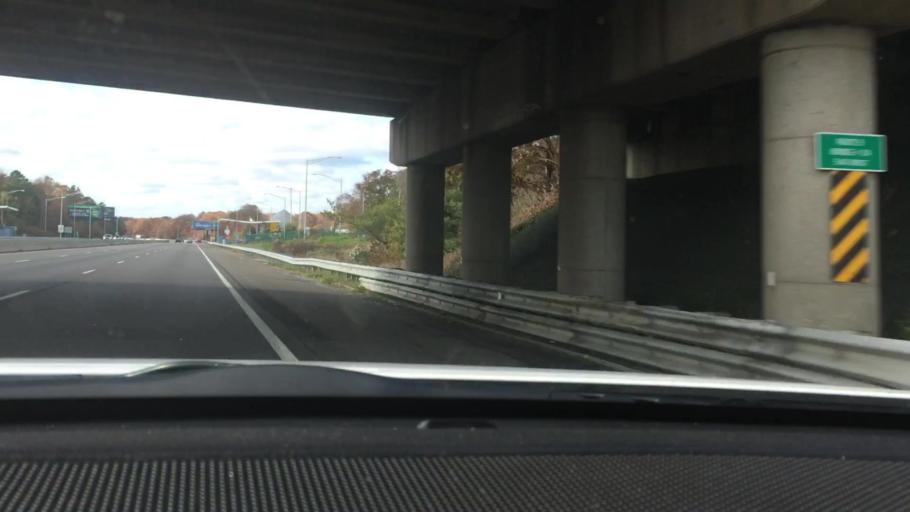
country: US
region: New Jersey
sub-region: Atlantic County
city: Pleasantville
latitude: 39.4022
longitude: -74.5241
